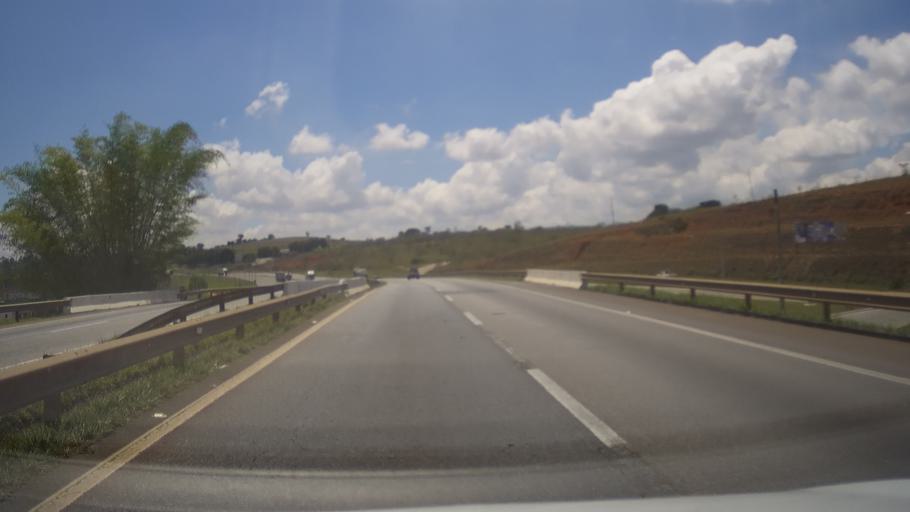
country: BR
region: Minas Gerais
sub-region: Sao Goncalo Do Sapucai
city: Sao Goncalo do Sapucai
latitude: -21.9143
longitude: -45.5789
